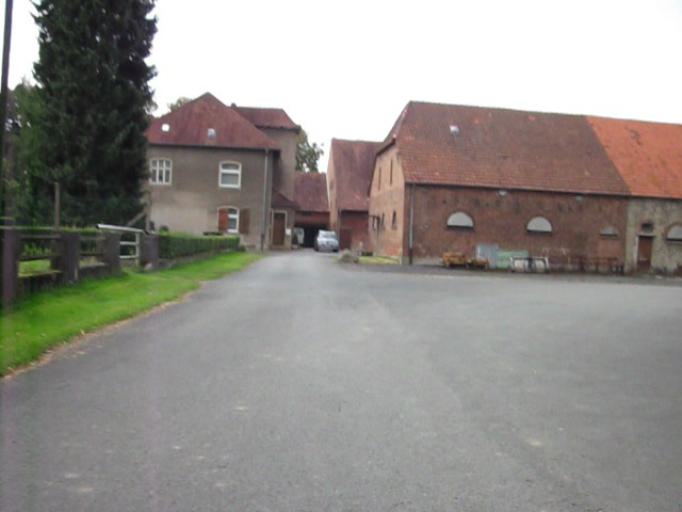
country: DE
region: North Rhine-Westphalia
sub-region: Regierungsbezirk Detmold
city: Paderborn
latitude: 51.7156
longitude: 8.7118
